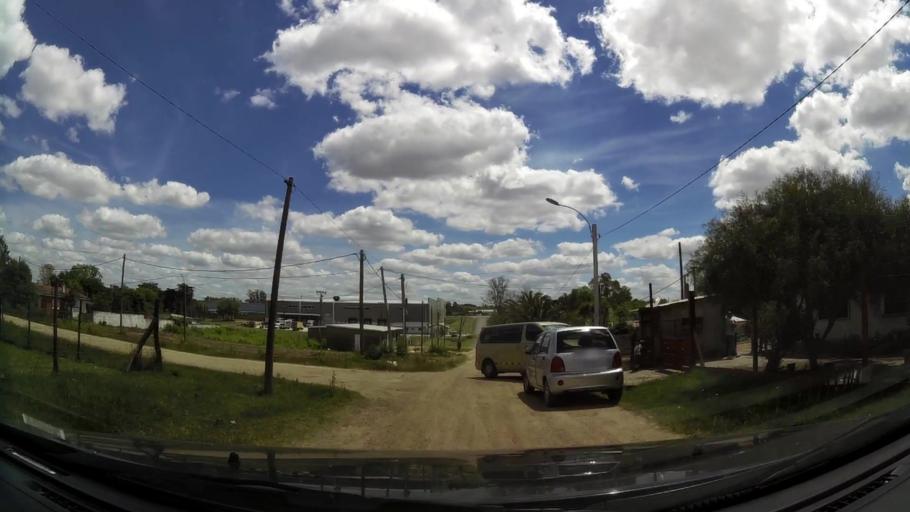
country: UY
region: Canelones
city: Colonia Nicolich
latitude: -34.8218
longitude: -56.0115
